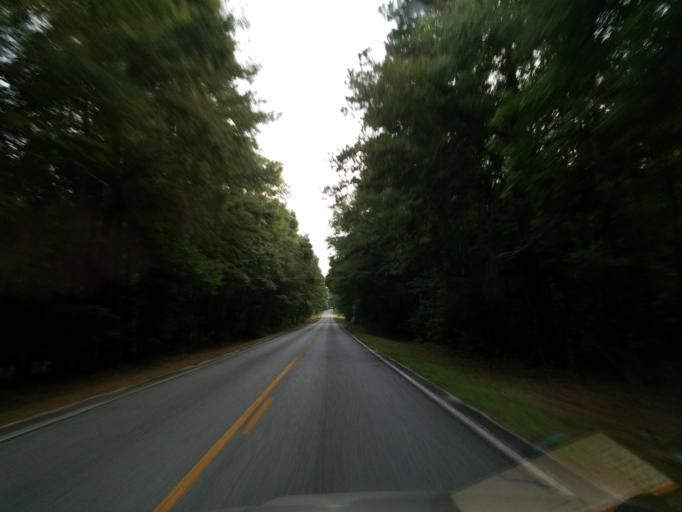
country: US
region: Mississippi
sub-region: Clarke County
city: Stonewall
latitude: 32.1102
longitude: -88.8565
